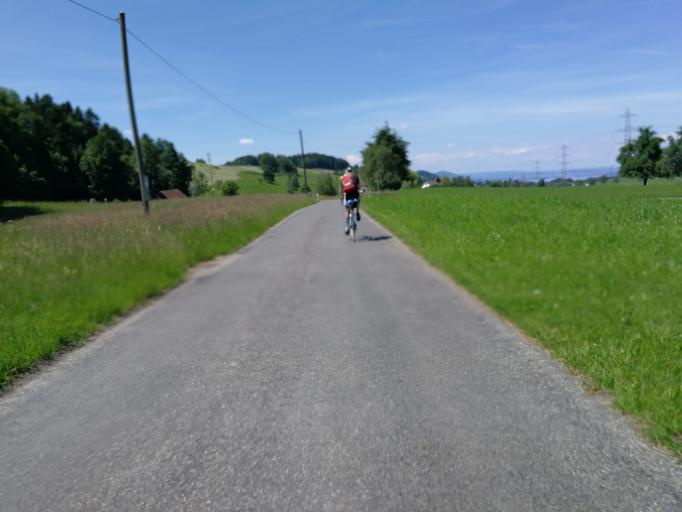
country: CH
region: Zurich
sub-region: Bezirk Horgen
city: Waedenswil / Hangenmoos
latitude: 47.2077
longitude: 8.6419
